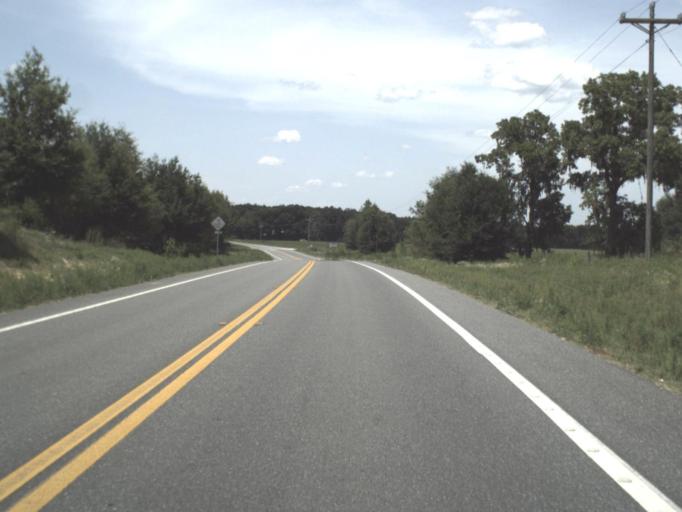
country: US
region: Florida
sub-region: Gilchrist County
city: Trenton
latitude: 29.8628
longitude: -82.8601
